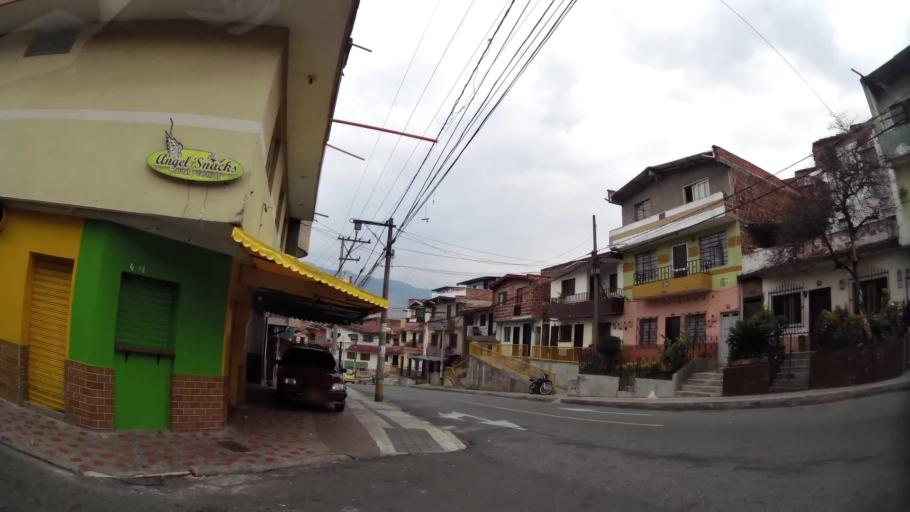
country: CO
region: Antioquia
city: Medellin
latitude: 6.2901
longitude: -75.5570
